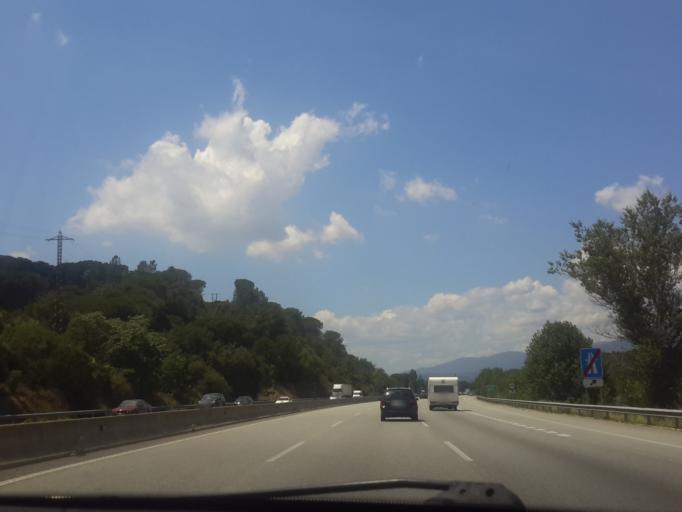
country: ES
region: Catalonia
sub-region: Provincia de Girona
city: Hostalric
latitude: 41.7261
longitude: 2.5998
